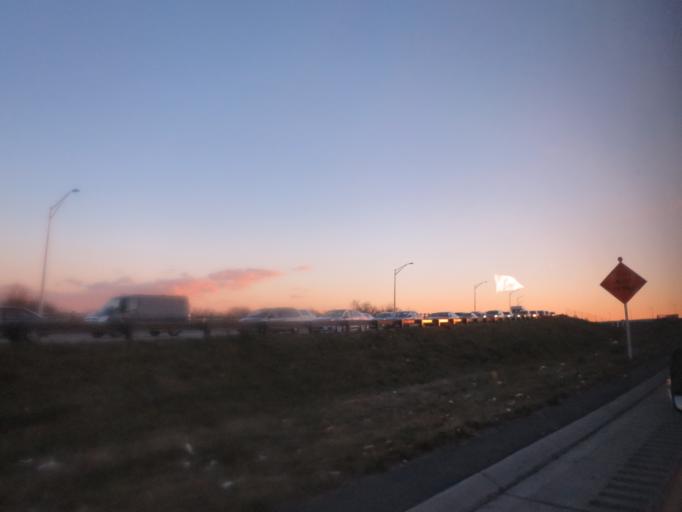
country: US
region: New York
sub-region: Kings County
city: East New York
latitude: 40.6248
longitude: -73.8946
